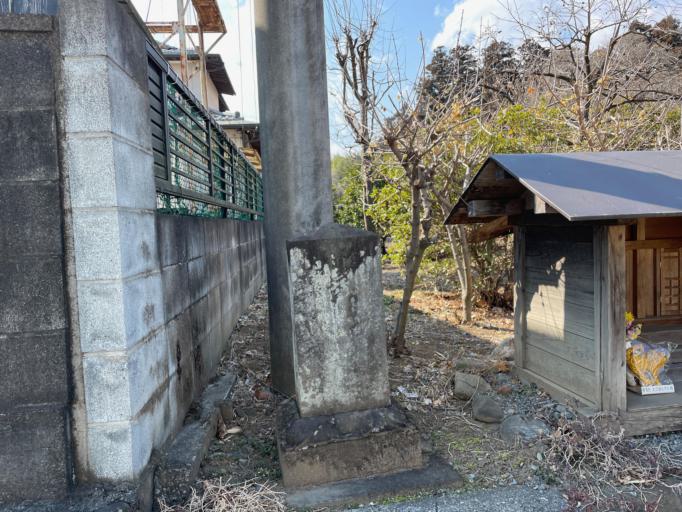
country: JP
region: Saitama
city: Yorii
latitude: 36.1133
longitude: 139.2358
